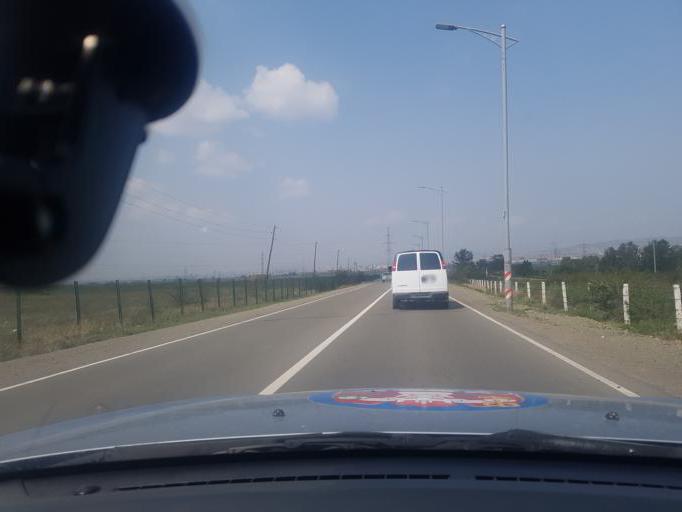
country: MN
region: Ulaanbaatar
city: Ulaanbaatar
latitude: 47.8898
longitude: 107.0430
